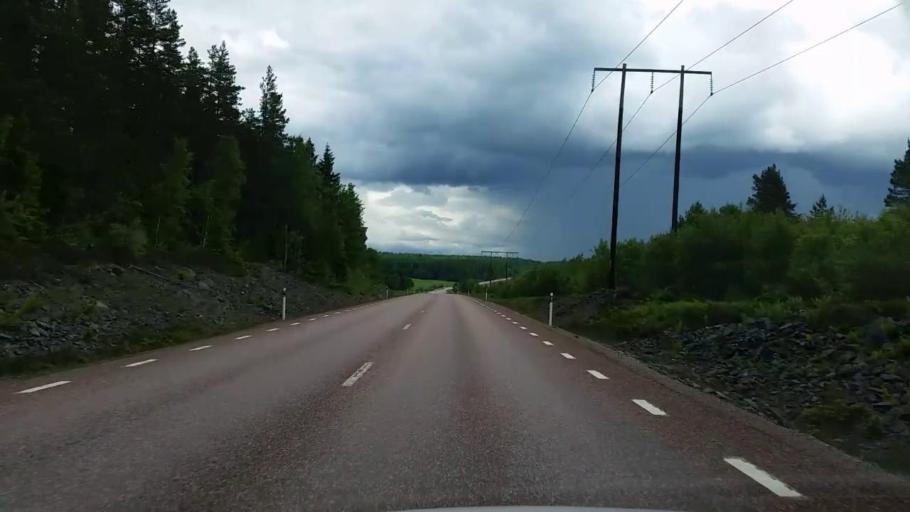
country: SE
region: Gaevleborg
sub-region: Hofors Kommun
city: Hofors
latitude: 60.5327
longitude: 16.4577
